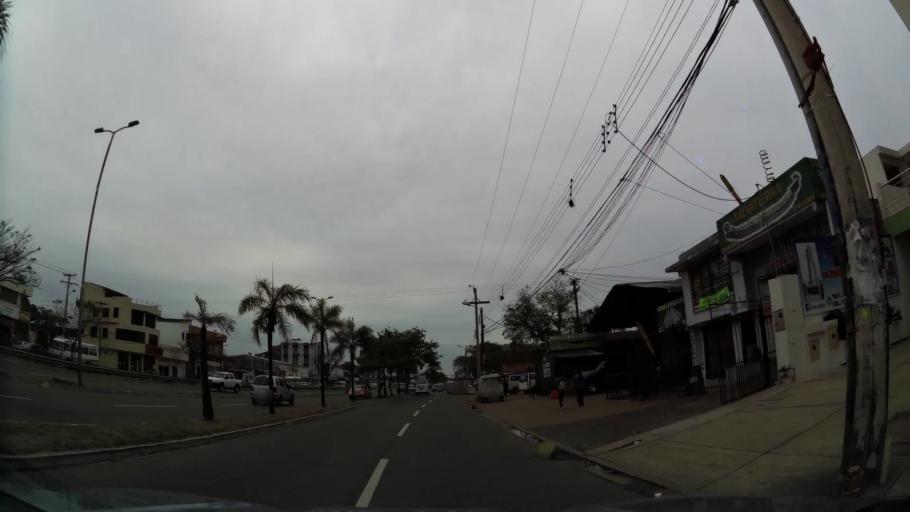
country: BO
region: Santa Cruz
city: Santa Cruz de la Sierra
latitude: -17.7999
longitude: -63.1909
